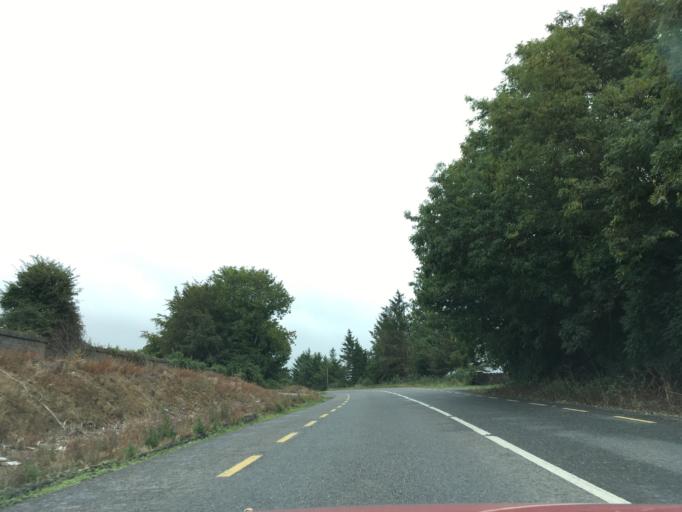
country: IE
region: Munster
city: Carrick-on-Suir
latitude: 52.3654
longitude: -7.5425
